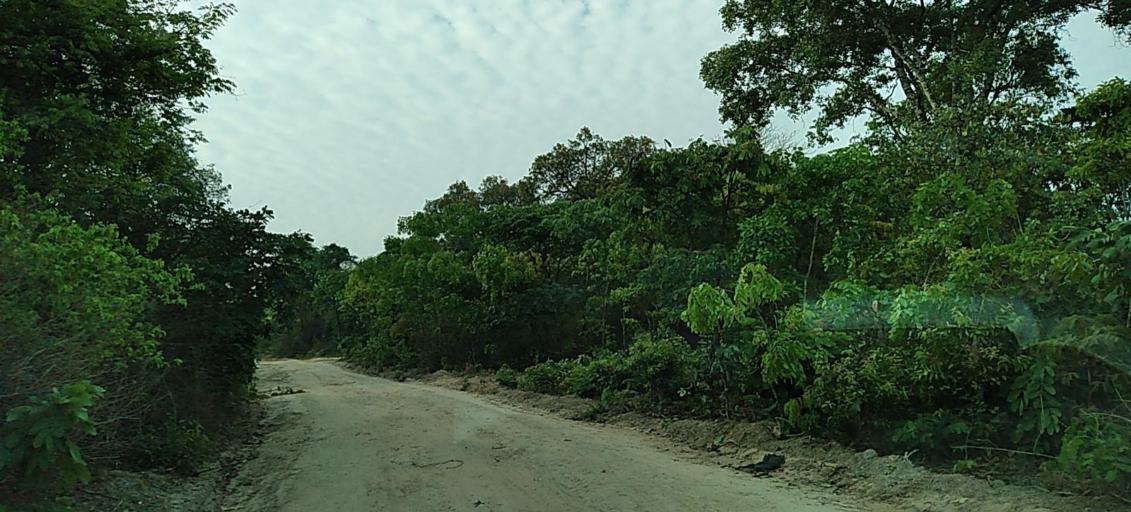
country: ZM
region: Copperbelt
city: Kalulushi
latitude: -12.8978
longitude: 27.6855
